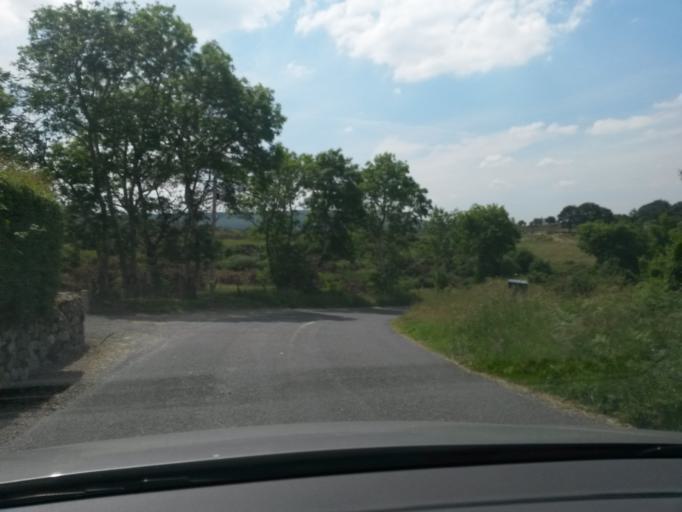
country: IE
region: Leinster
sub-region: Wicklow
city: Blessington
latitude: 53.1706
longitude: -6.4562
